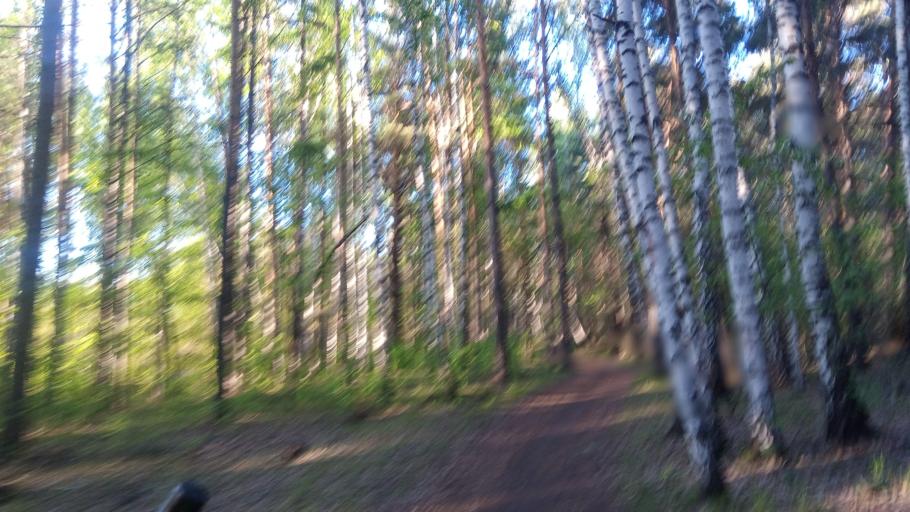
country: RU
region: Chelyabinsk
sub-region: Gorod Chelyabinsk
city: Chelyabinsk
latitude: 55.1497
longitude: 61.3306
